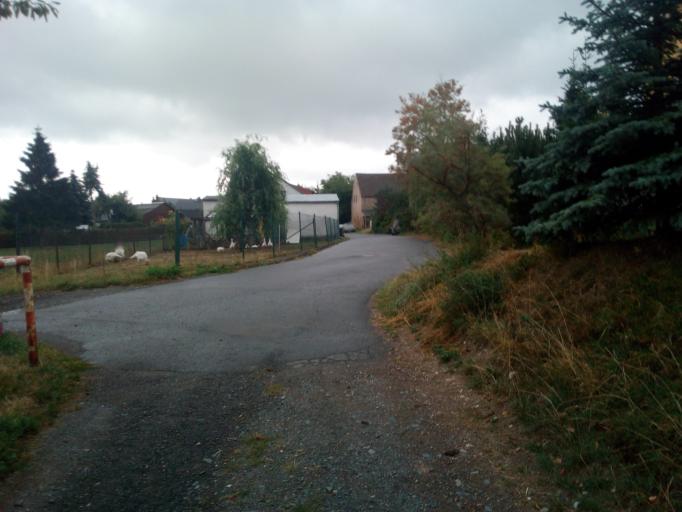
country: DE
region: Saxony
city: Kreischa
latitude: 50.9264
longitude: 13.7973
